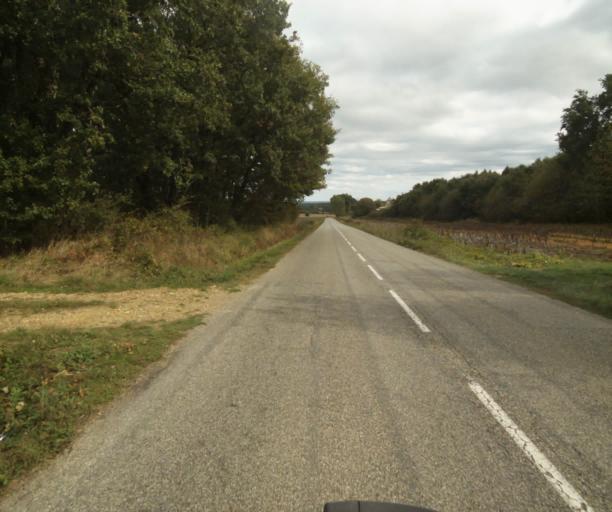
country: FR
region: Midi-Pyrenees
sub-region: Departement du Tarn-et-Garonne
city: Verdun-sur-Garonne
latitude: 43.8579
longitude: 1.1196
